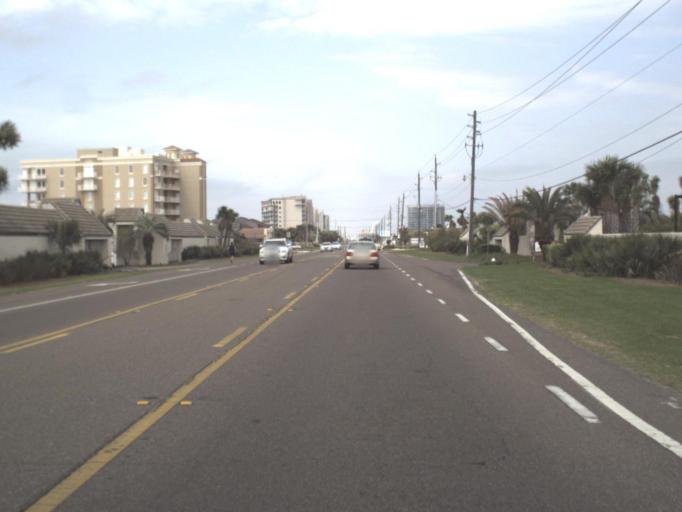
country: US
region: Alabama
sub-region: Baldwin County
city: Orange Beach
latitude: 30.2838
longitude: -87.5077
